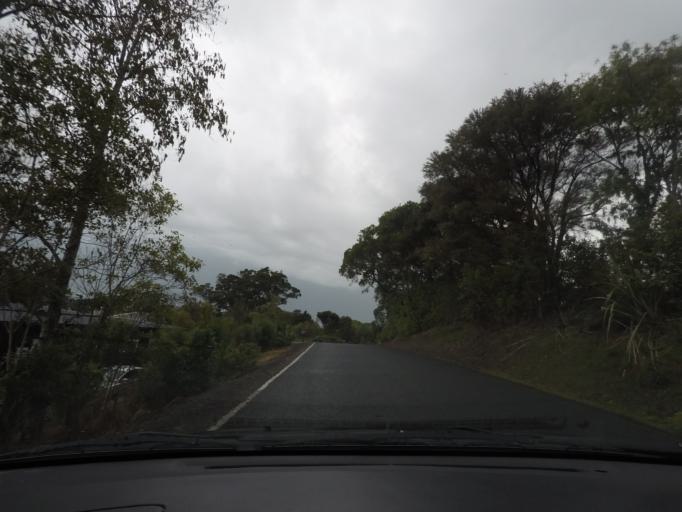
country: NZ
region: Auckland
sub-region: Auckland
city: Warkworth
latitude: -36.4752
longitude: 174.7336
